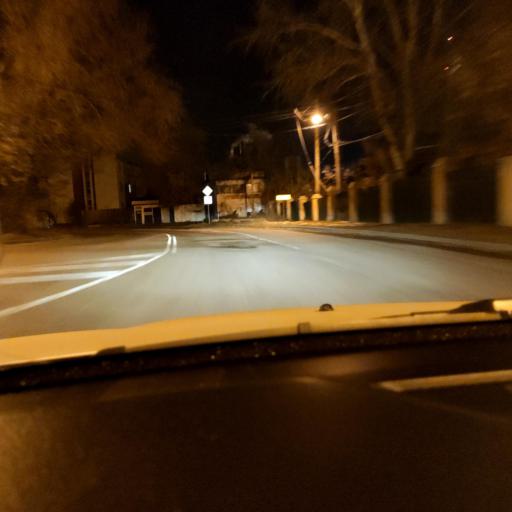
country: RU
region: Samara
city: Rozhdestveno
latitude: 53.1764
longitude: 50.0798
